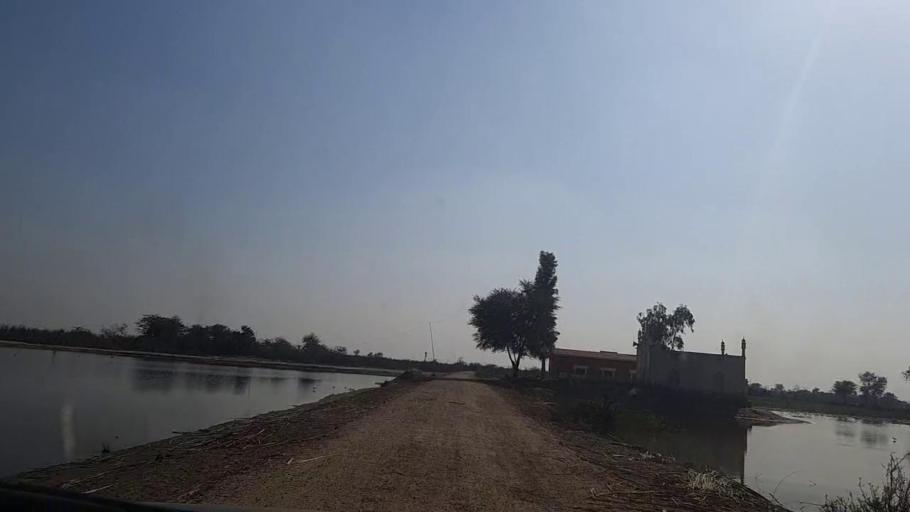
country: PK
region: Sindh
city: Sakrand
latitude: 26.0872
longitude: 68.3704
